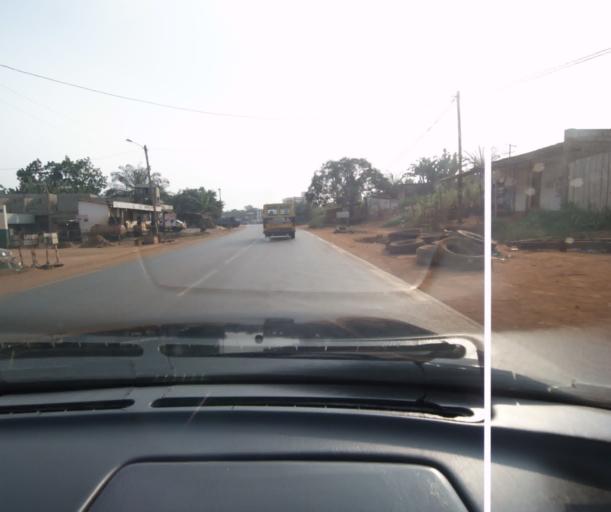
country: CM
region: Centre
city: Okoa
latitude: 3.9670
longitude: 11.5423
